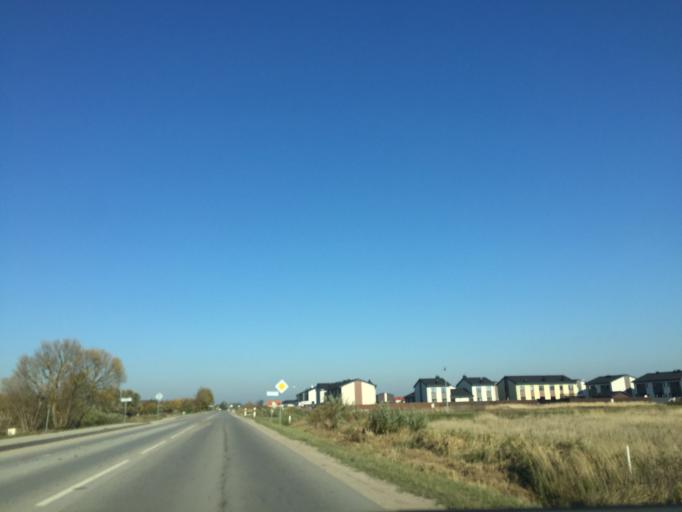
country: LT
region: Klaipedos apskritis
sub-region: Klaipeda
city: Klaipeda
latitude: 55.7388
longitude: 21.1927
